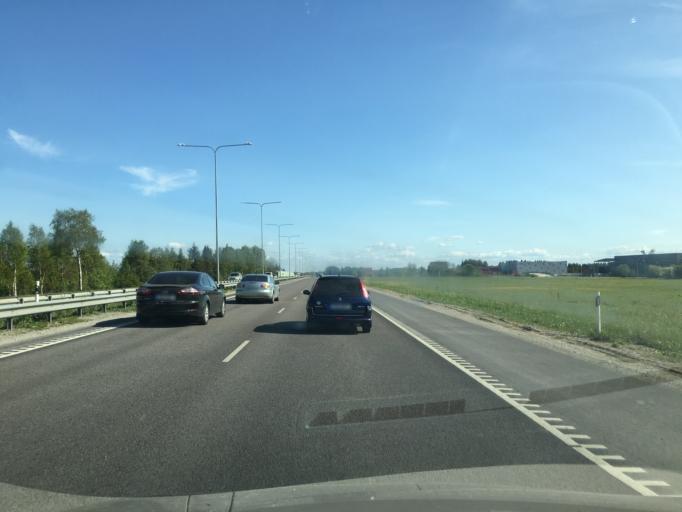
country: EE
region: Harju
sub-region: Rae vald
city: Jueri
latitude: 59.3909
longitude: 24.8271
